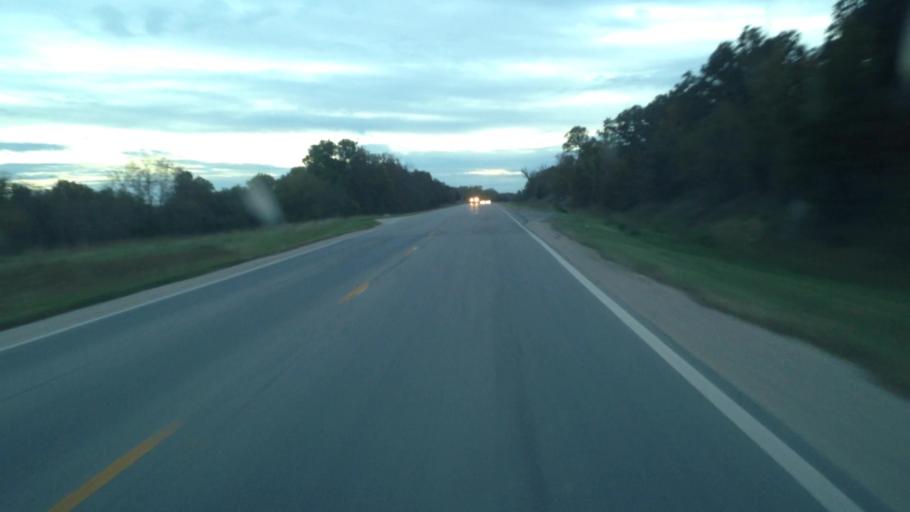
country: US
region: Kansas
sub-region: Anderson County
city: Garnett
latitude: 38.2089
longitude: -95.2490
